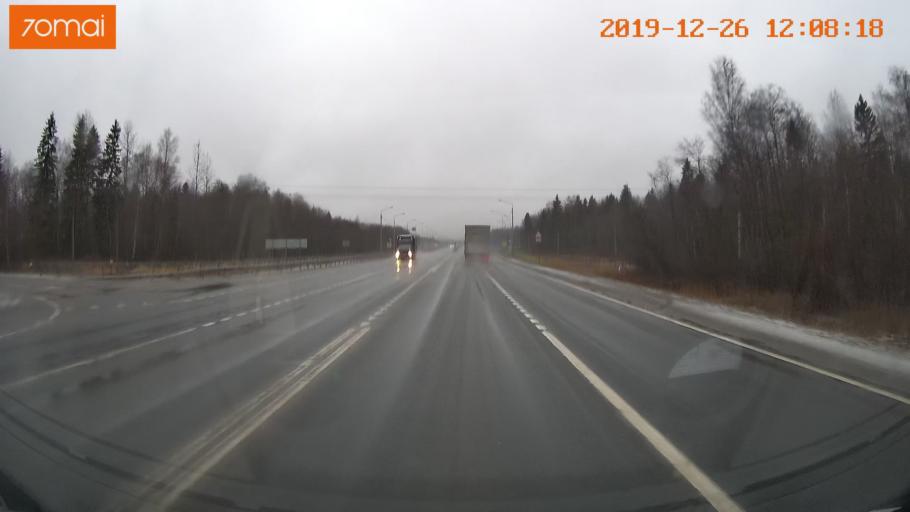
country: RU
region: Vologda
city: Tonshalovo
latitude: 59.2838
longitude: 38.0158
